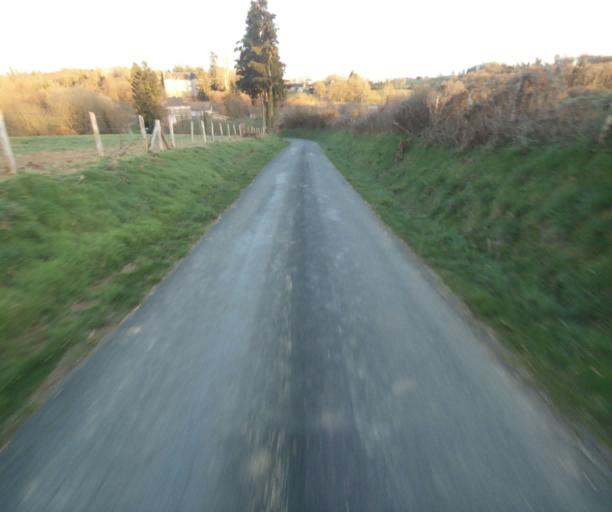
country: FR
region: Limousin
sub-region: Departement de la Correze
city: Uzerche
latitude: 45.3681
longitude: 1.6154
